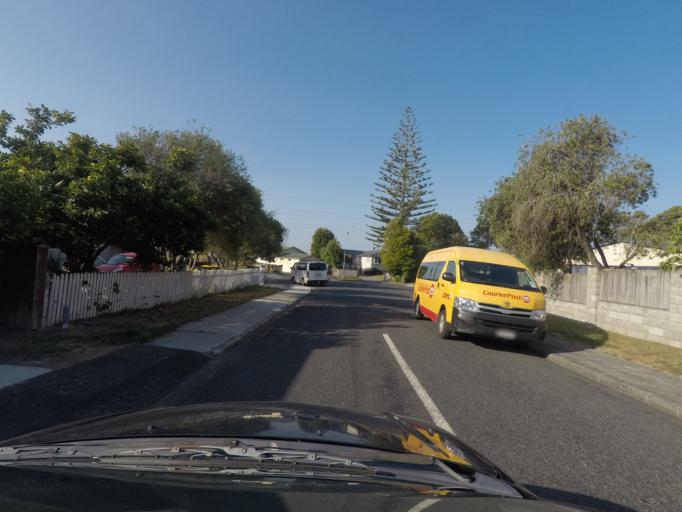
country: NZ
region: Auckland
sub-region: Auckland
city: Rosebank
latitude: -36.8574
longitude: 174.6487
